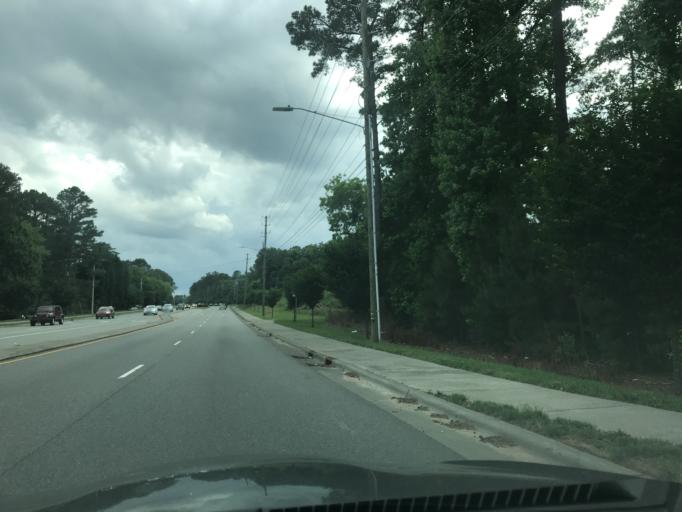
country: US
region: North Carolina
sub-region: Wake County
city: Wake Forest
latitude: 35.9233
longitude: -78.5899
